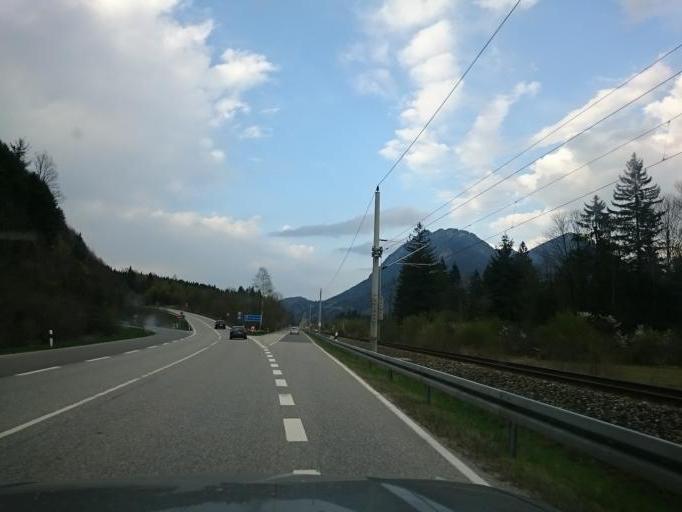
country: DE
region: Bavaria
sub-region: Upper Bavaria
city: Eschenlohe
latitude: 47.5865
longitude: 11.1739
